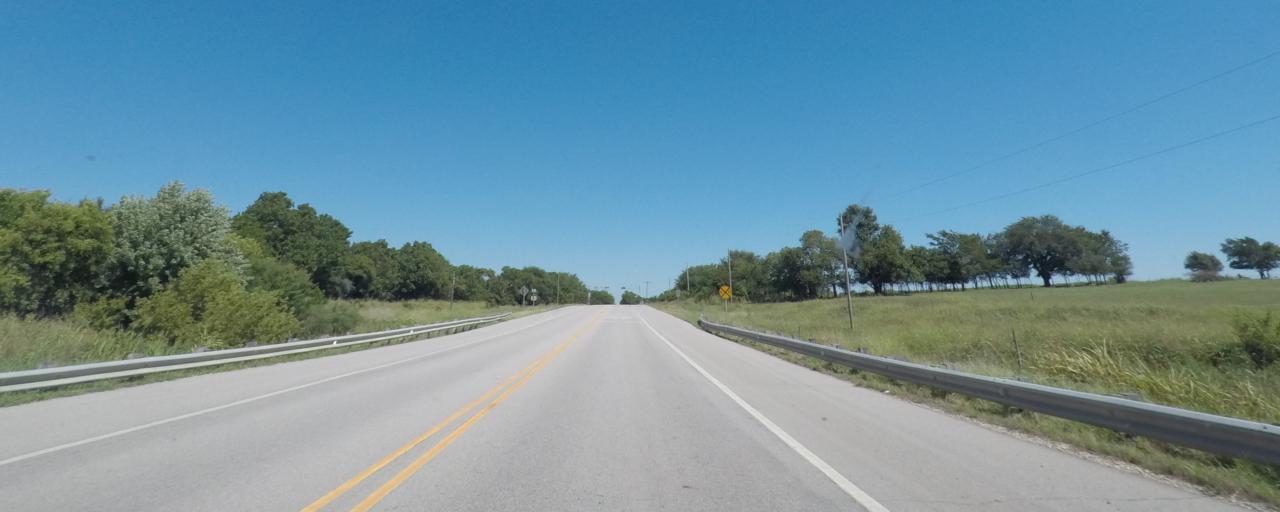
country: US
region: Kansas
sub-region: Sumner County
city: Caldwell
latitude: 37.0594
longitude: -97.4013
